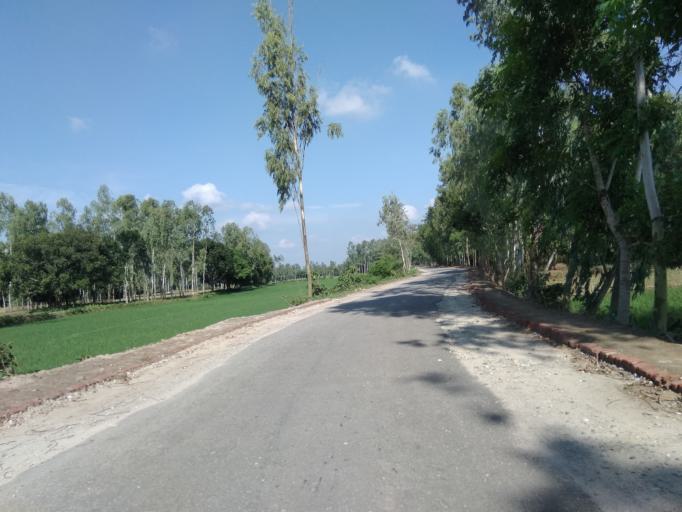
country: BD
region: Rangpur Division
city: Panchagarh
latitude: 26.2557
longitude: 88.6173
